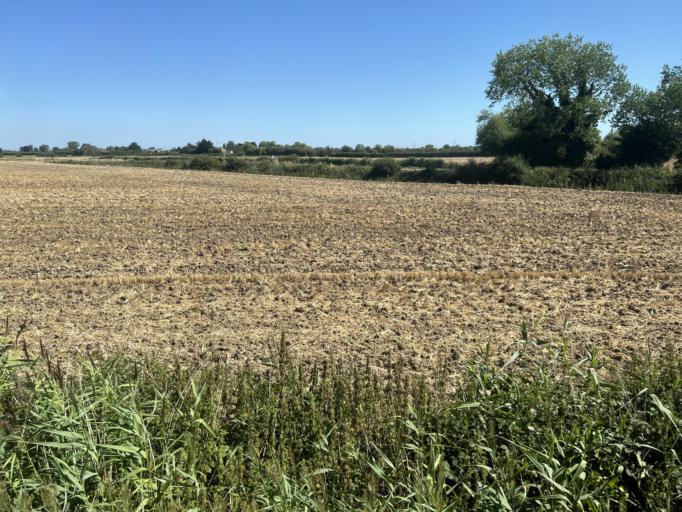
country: GB
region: England
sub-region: Lincolnshire
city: Wainfleet All Saints
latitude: 53.1241
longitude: 0.1984
